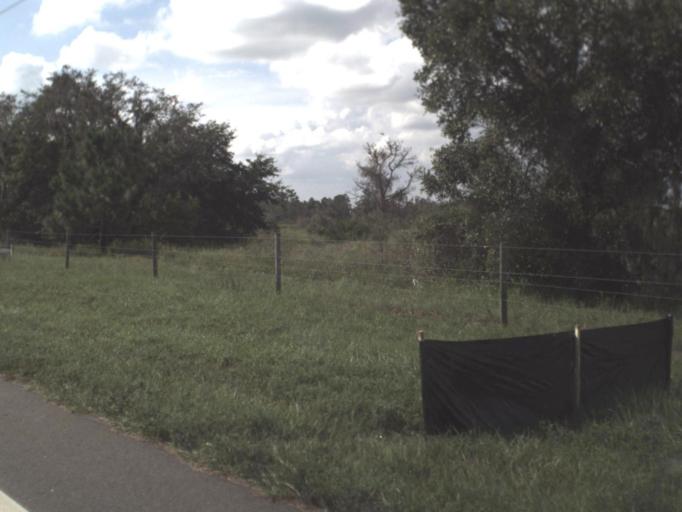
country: US
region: Florida
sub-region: Sarasota County
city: The Meadows
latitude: 27.4749
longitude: -82.3272
